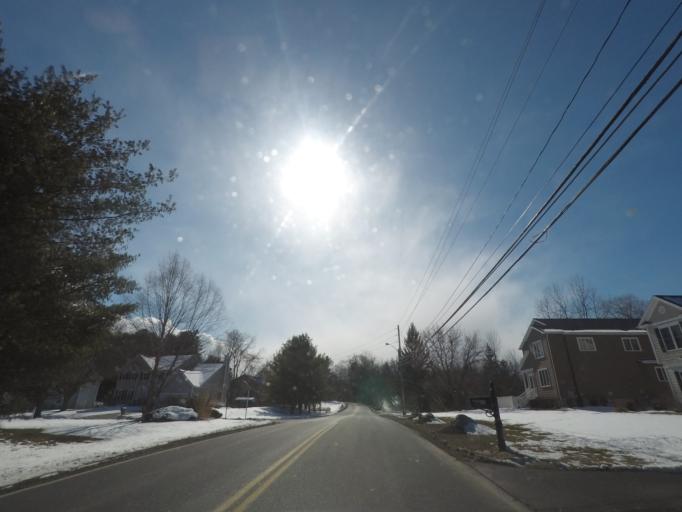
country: US
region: New York
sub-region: Albany County
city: McKownville
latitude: 42.6615
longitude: -73.8447
